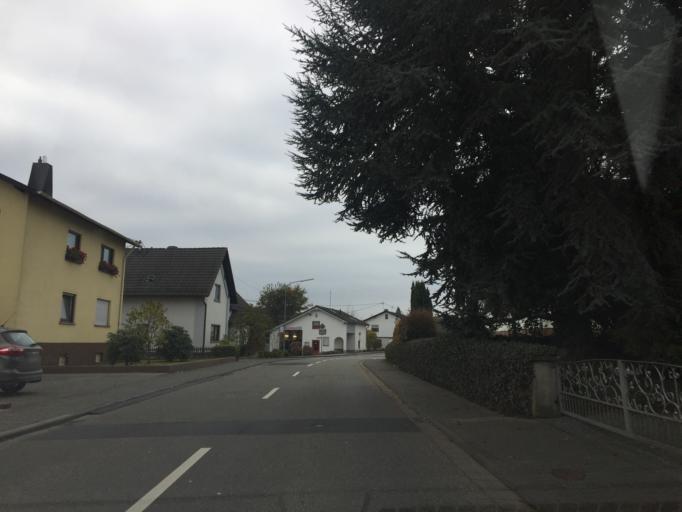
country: DE
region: Rheinland-Pfalz
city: Girod
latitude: 50.4475
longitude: 7.9055
